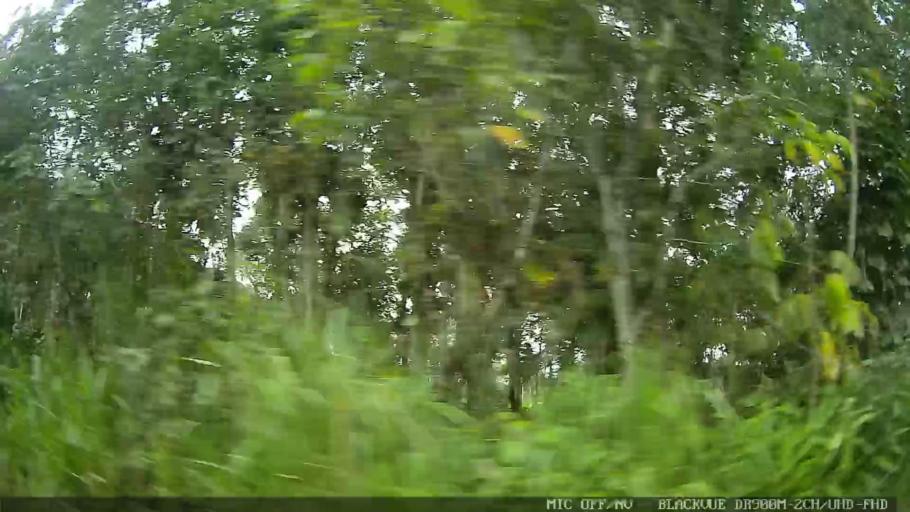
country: BR
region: Sao Paulo
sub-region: Itanhaem
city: Itanhaem
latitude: -24.0982
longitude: -46.8016
